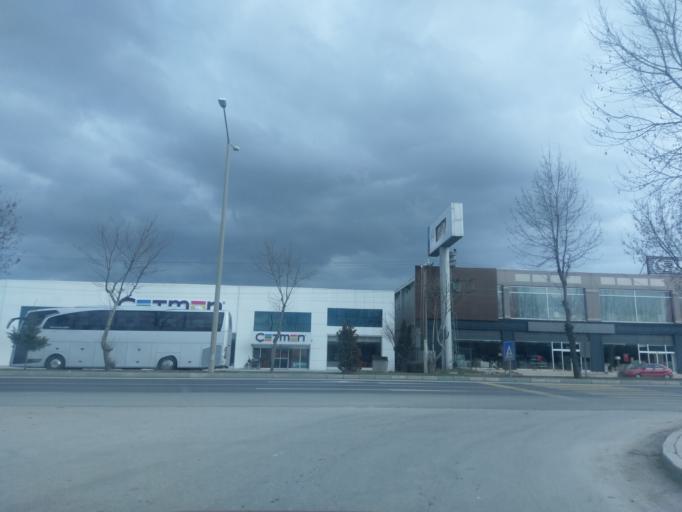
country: TR
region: Kuetahya
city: Kutahya
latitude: 39.4359
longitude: 29.9984
